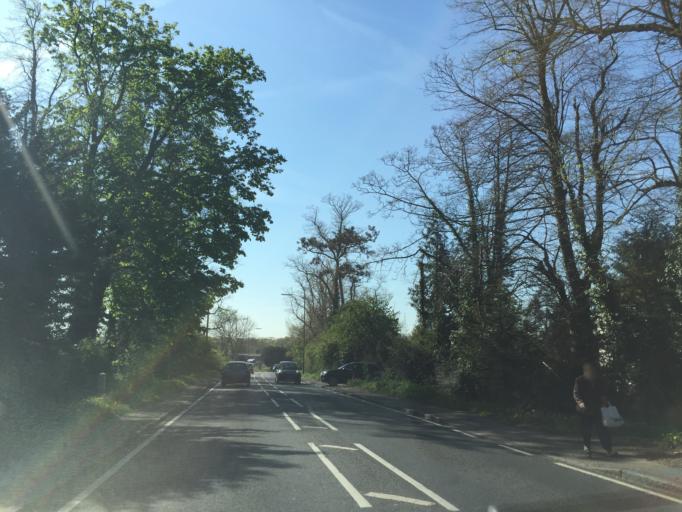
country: GB
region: England
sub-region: Essex
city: Epping
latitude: 51.7232
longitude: 0.1275
